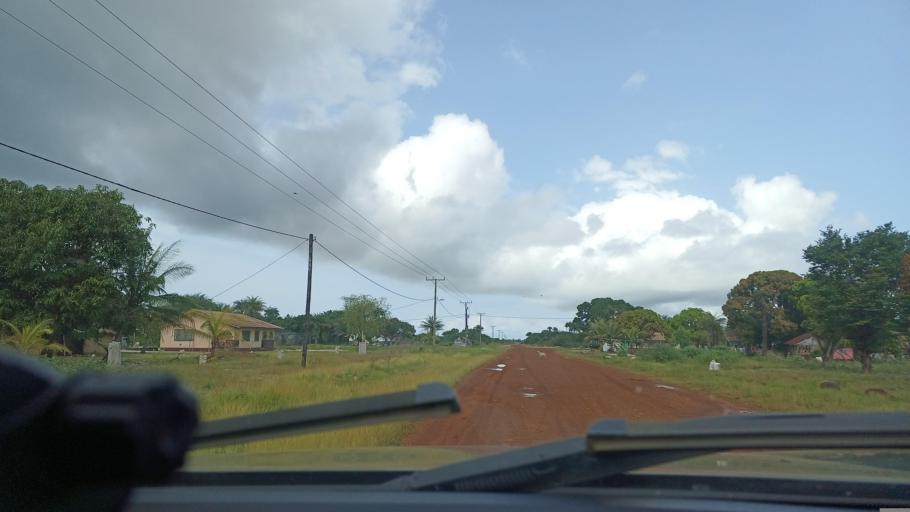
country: LR
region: Grand Cape Mount
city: Robertsport
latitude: 6.6913
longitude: -11.2669
